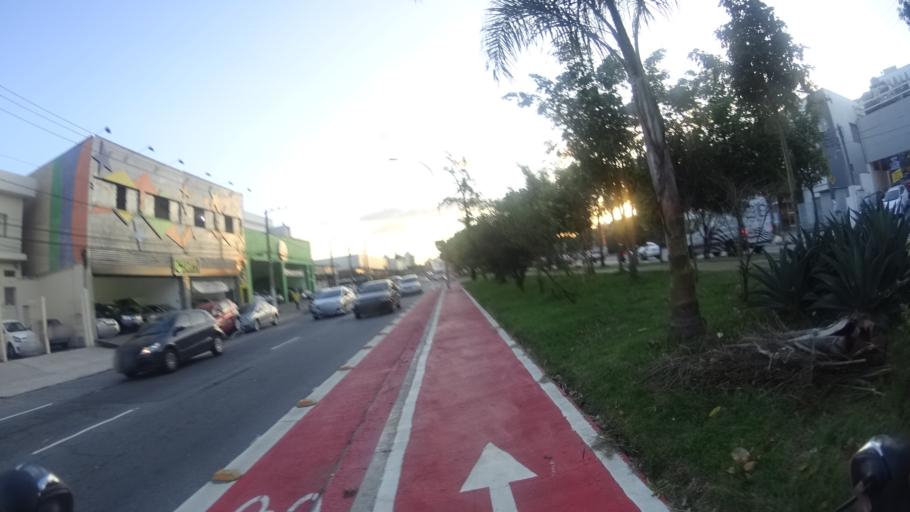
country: BR
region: Sao Paulo
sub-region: Sao Paulo
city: Sao Paulo
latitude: -23.4885
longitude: -46.6503
